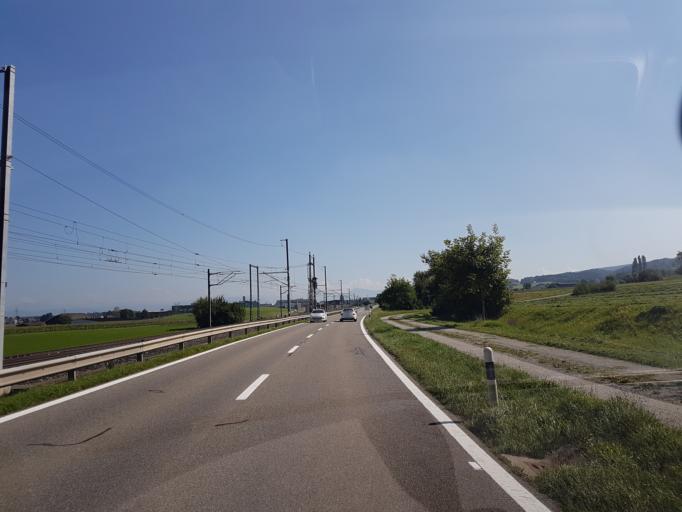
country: CH
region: Aargau
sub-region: Bezirk Muri
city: Waltenschwil
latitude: 47.3144
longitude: 8.3063
